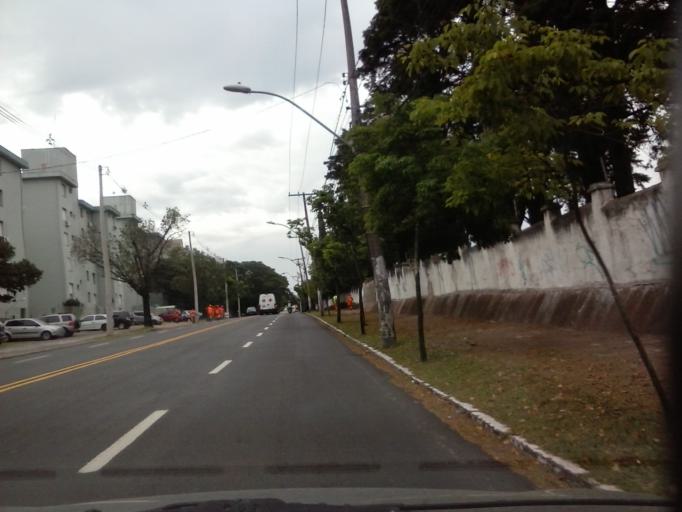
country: BR
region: Rio Grande do Sul
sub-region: Porto Alegre
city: Porto Alegre
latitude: -30.0594
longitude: -51.2080
